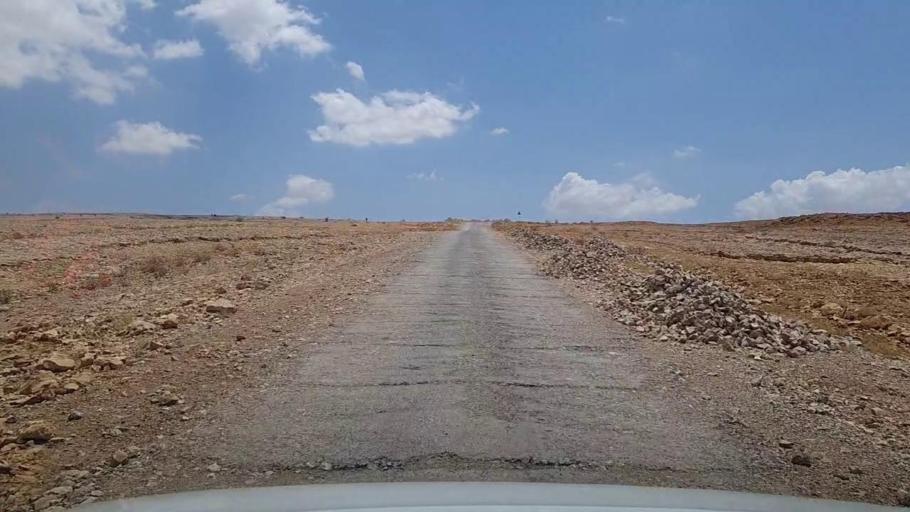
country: PK
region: Sindh
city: Bhan
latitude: 26.2898
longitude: 67.5800
